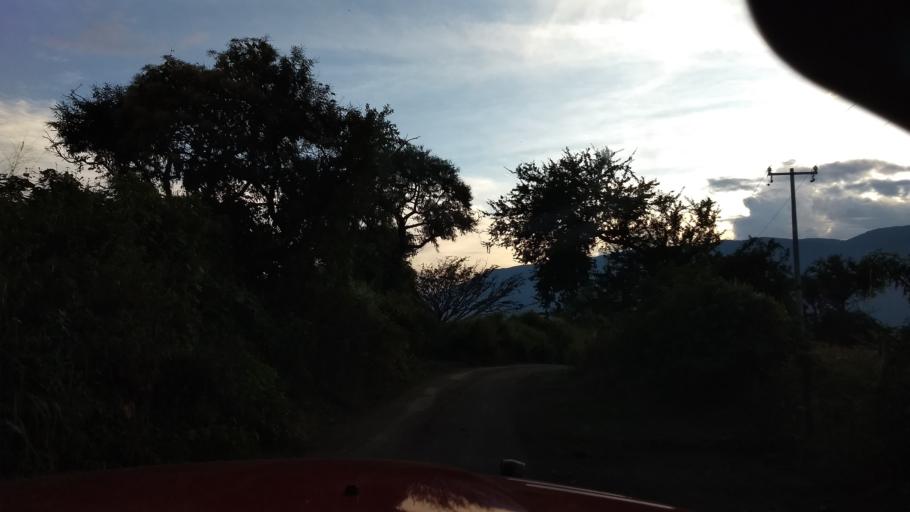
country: MX
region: Colima
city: Suchitlan
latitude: 19.4862
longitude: -103.7926
